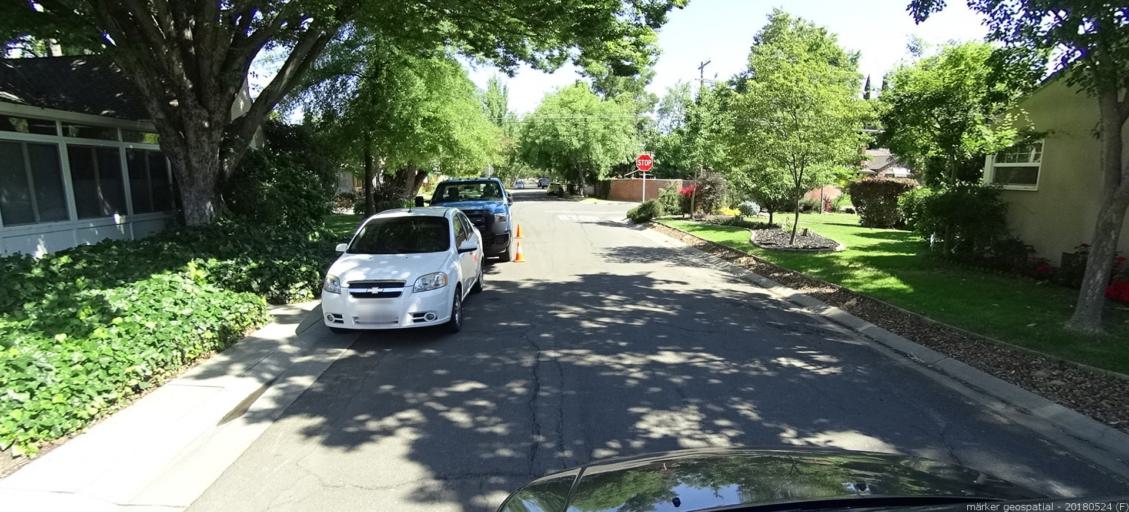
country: US
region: California
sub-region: Sacramento County
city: Sacramento
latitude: 38.6046
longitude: -121.4520
